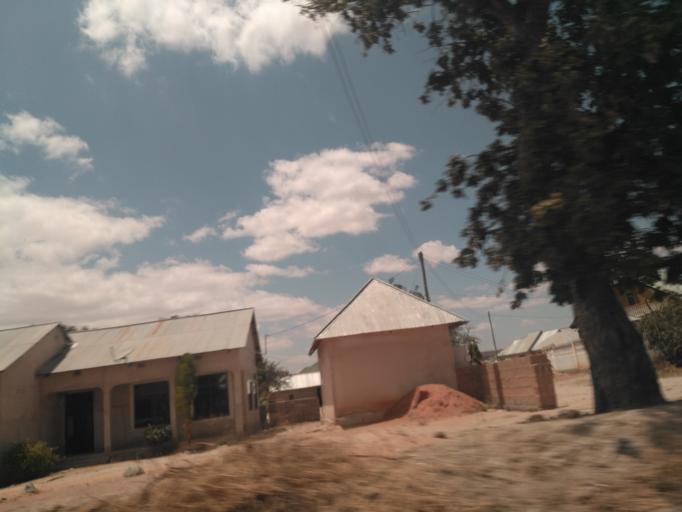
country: TZ
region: Dodoma
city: Kisasa
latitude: -6.1732
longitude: 35.7969
